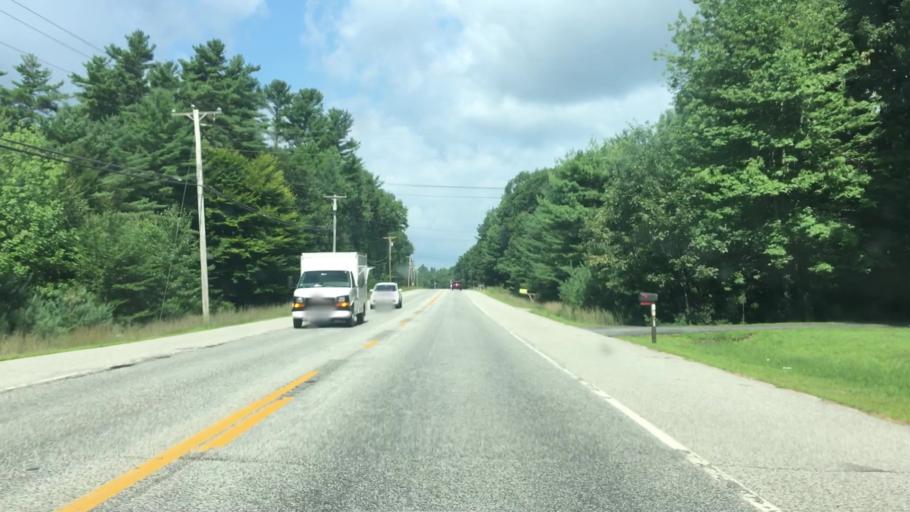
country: US
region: Maine
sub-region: Cumberland County
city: Raymond
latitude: 43.9039
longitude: -70.4830
